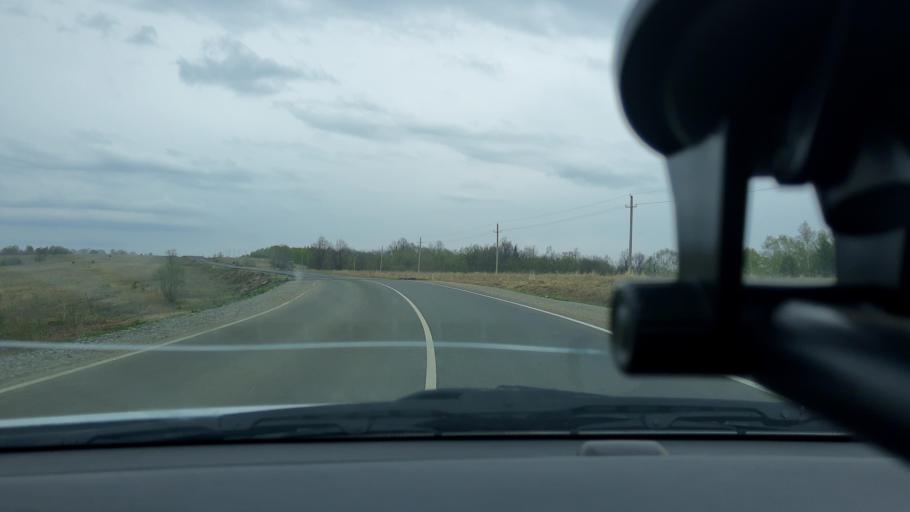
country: RU
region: Bashkortostan
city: Pavlovka
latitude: 55.3552
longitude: 56.4031
